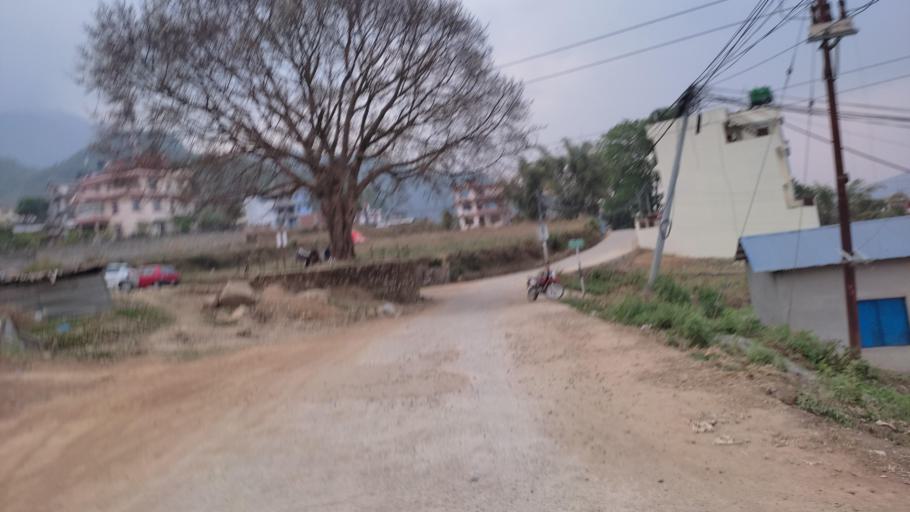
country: NP
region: Central Region
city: Kirtipur
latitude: 27.6711
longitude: 85.2438
